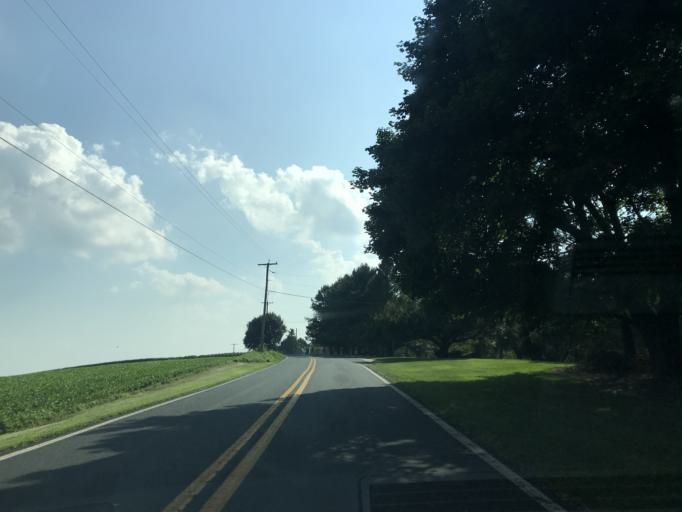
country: US
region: Maryland
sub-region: Carroll County
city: Westminster
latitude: 39.6216
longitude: -76.9756
